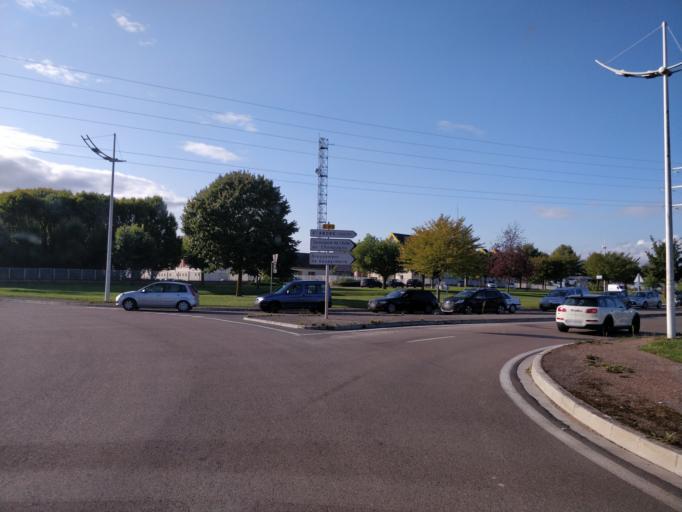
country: FR
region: Champagne-Ardenne
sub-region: Departement de l'Aube
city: Rosieres-pres-Troyes
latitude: 48.2680
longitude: 4.0619
